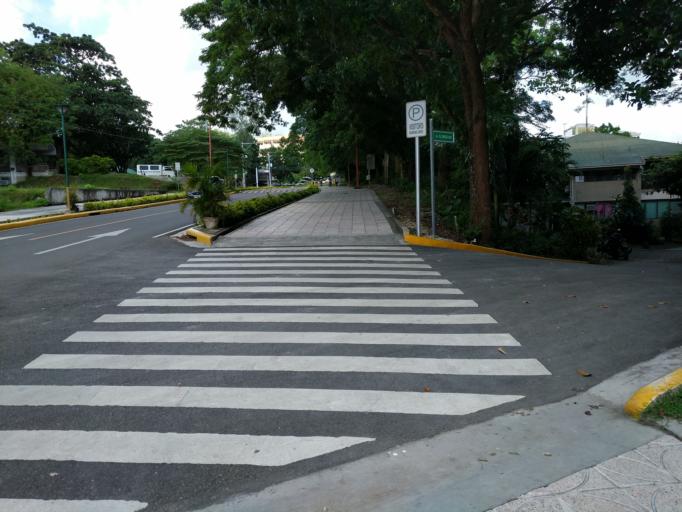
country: PH
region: Central Visayas
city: Mandaue City
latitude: 10.3540
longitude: 123.9131
